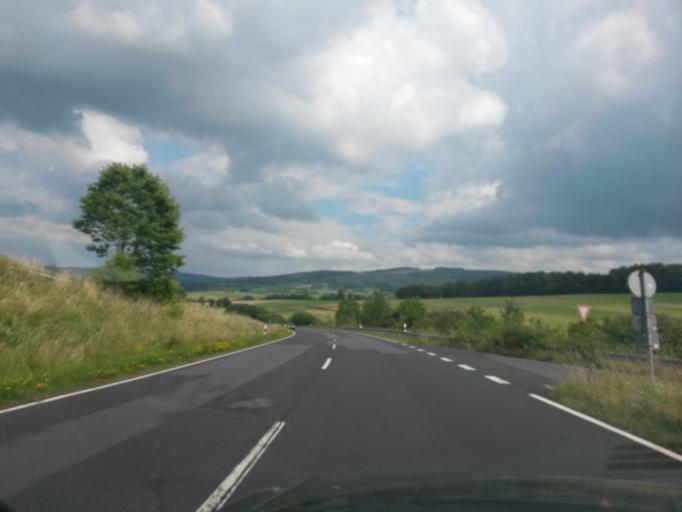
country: DE
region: Hesse
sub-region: Regierungsbezirk Kassel
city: Hilders
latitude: 50.5287
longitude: 9.9372
